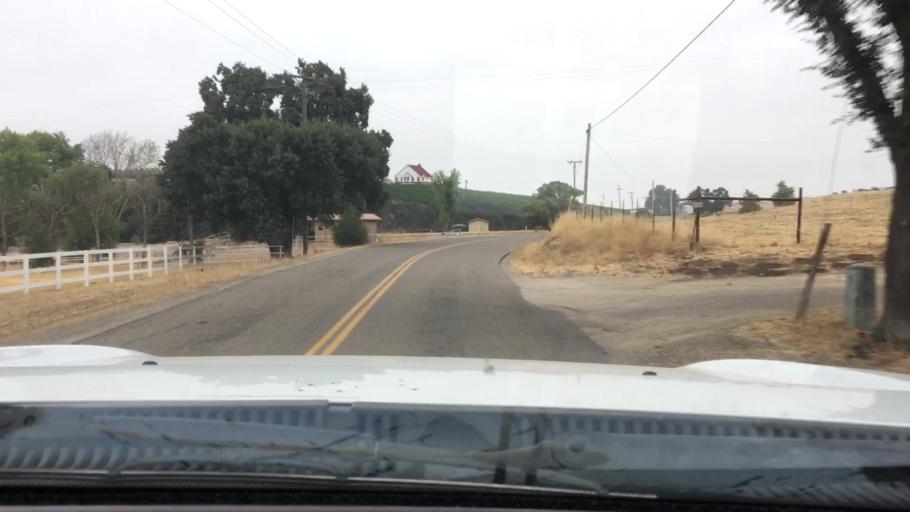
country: US
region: California
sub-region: San Luis Obispo County
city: Atascadero
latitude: 35.5352
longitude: -120.6137
